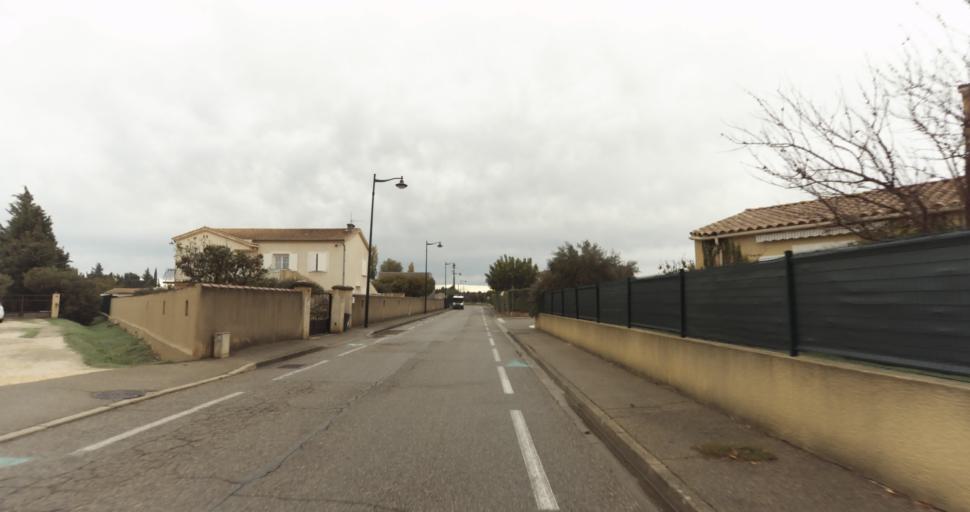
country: FR
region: Provence-Alpes-Cote d'Azur
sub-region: Departement des Bouches-du-Rhone
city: Rognonas
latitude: 43.9036
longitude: 4.7981
